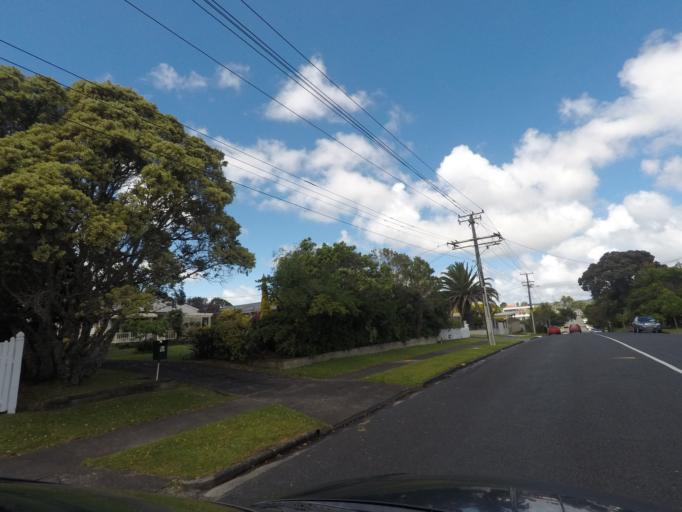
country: NZ
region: Auckland
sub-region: Auckland
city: Rosebank
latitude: -36.8788
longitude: 174.6418
